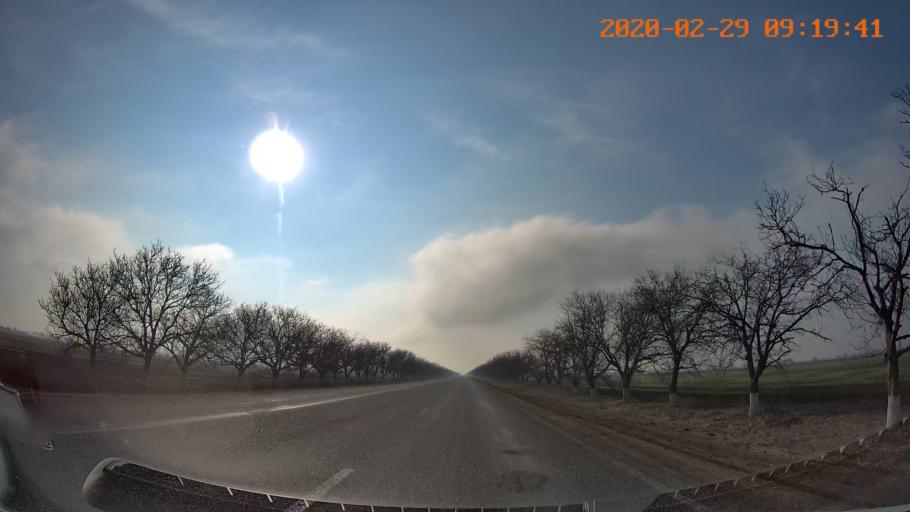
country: MD
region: Telenesti
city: Pervomaisc
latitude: 46.7595
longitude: 29.9413
